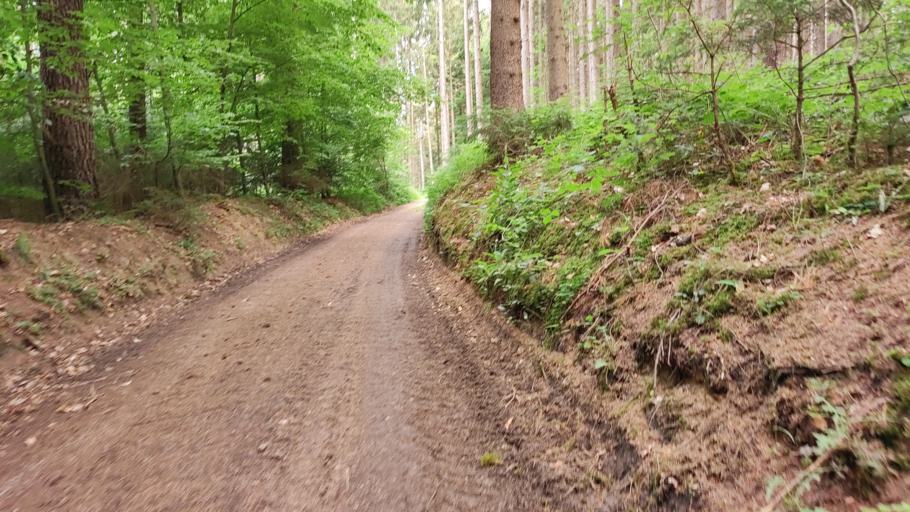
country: DE
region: Bavaria
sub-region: Swabia
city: Horgau
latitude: 48.4118
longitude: 10.6950
